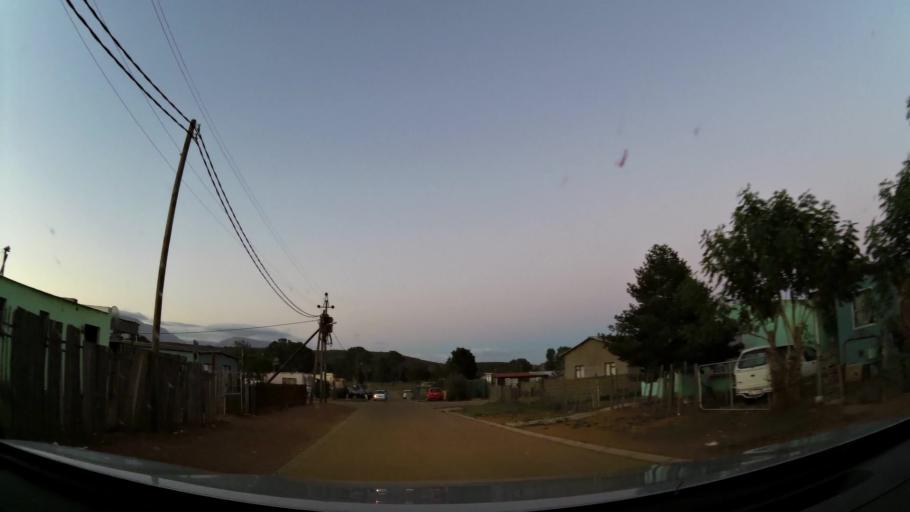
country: ZA
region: Western Cape
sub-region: Eden District Municipality
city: Riversdale
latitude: -34.1008
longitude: 21.2697
